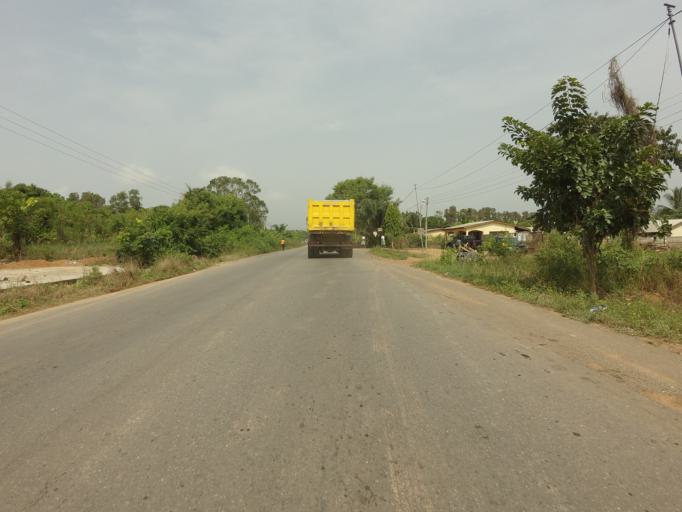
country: GH
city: Akropong
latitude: 6.2496
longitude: 0.0851
